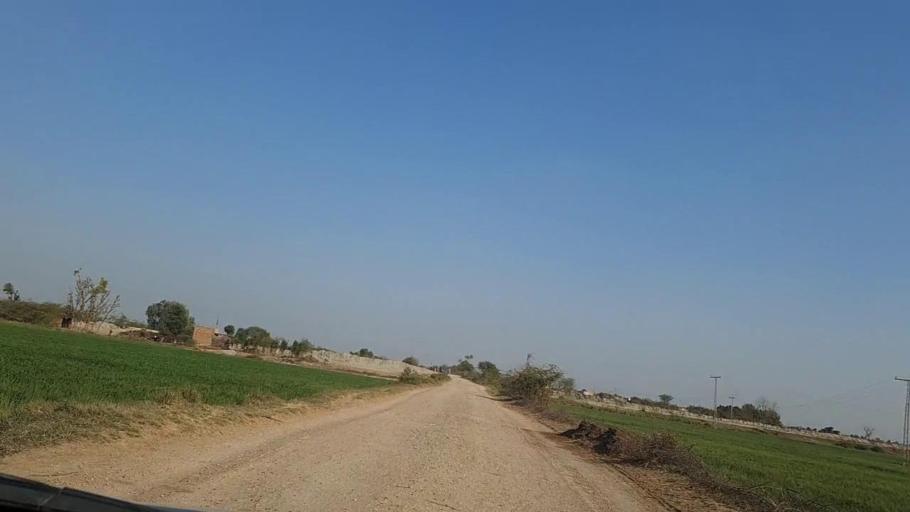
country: PK
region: Sindh
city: Sakrand
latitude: 26.0207
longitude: 68.3279
